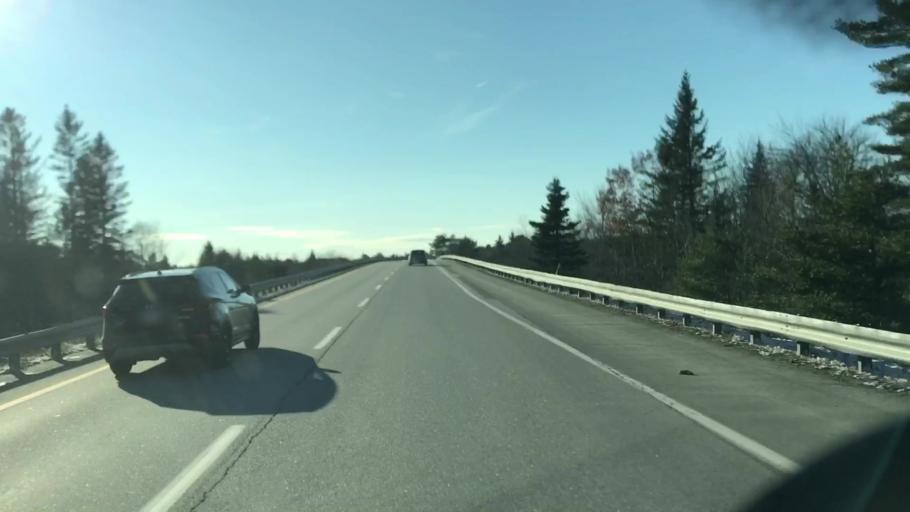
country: US
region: Maine
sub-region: Penobscot County
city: Hampden
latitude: 44.7717
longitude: -68.8668
